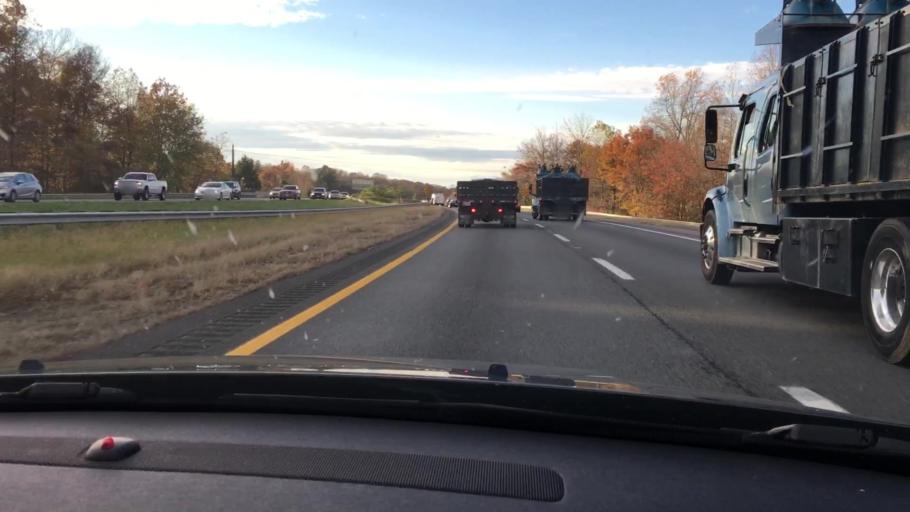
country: US
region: Maryland
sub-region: Anne Arundel County
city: Crownsville
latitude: 38.9962
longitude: -76.5852
